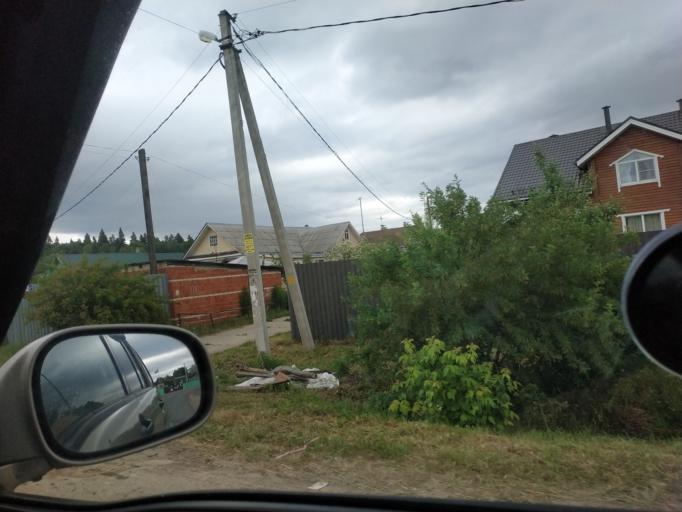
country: RU
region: Moskovskaya
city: Chernogolovka
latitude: 56.0672
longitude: 38.2589
